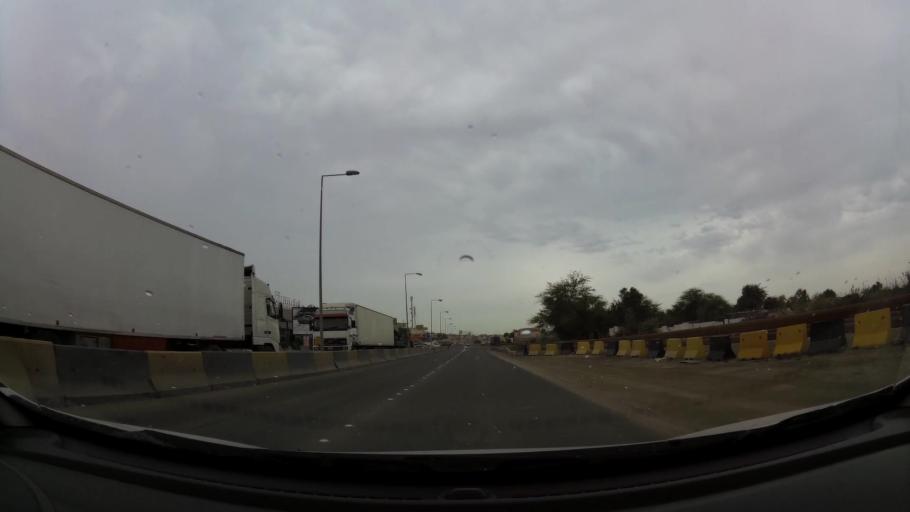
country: BH
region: Central Governorate
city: Madinat Hamad
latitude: 26.1474
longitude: 50.4893
